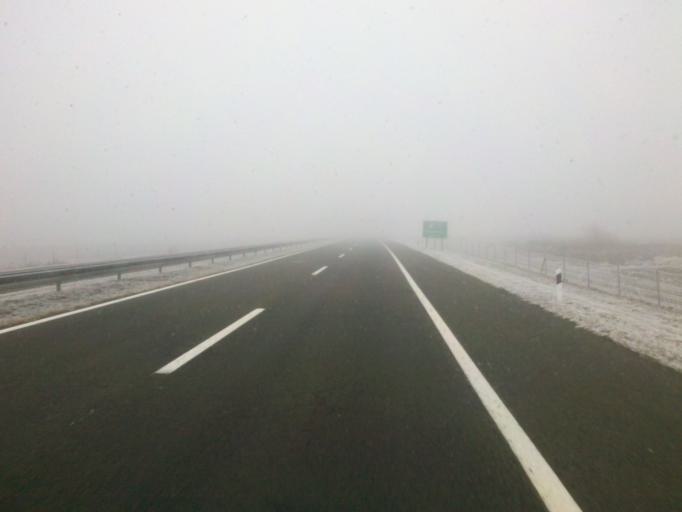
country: HR
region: Medimurska
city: Orehovica
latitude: 46.3313
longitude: 16.5232
